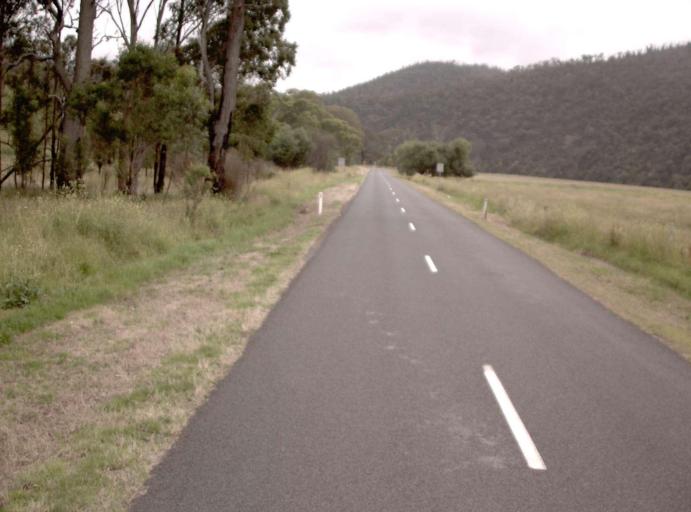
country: AU
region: Victoria
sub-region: Wellington
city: Heyfield
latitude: -37.7961
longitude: 146.6758
